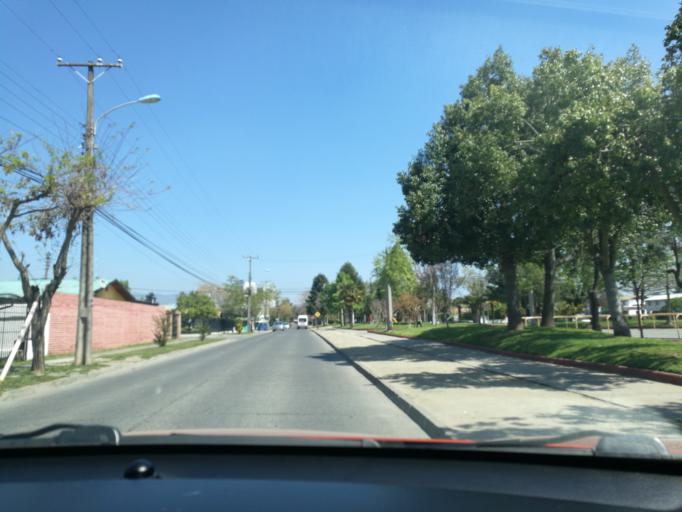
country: CL
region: O'Higgins
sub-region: Provincia de Cachapoal
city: Rancagua
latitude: -34.1597
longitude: -70.7359
